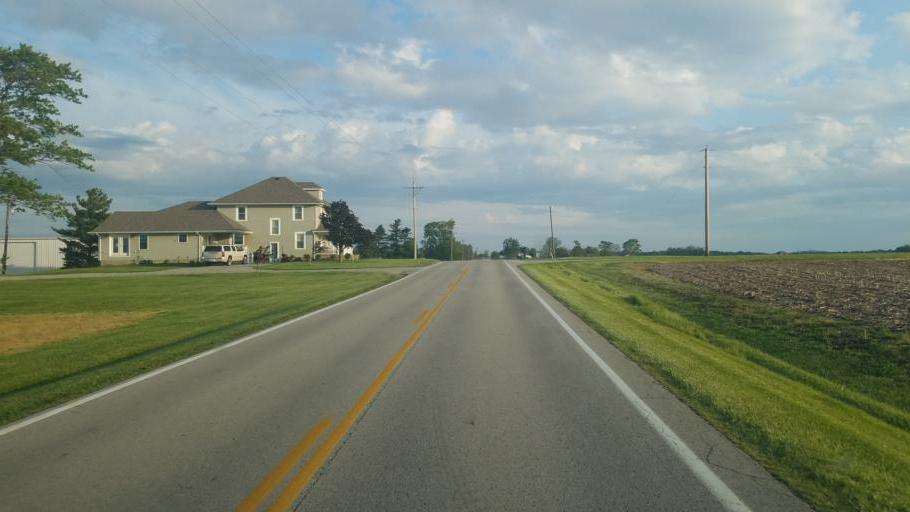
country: US
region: Ohio
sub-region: Highland County
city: Leesburg
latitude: 39.4047
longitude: -83.6039
